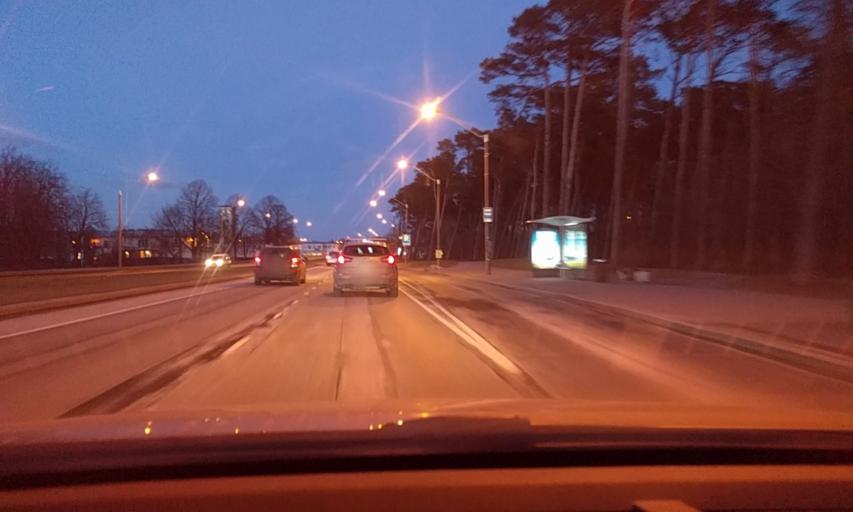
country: EE
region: Harju
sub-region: Viimsi vald
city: Viimsi
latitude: 59.4641
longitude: 24.8289
